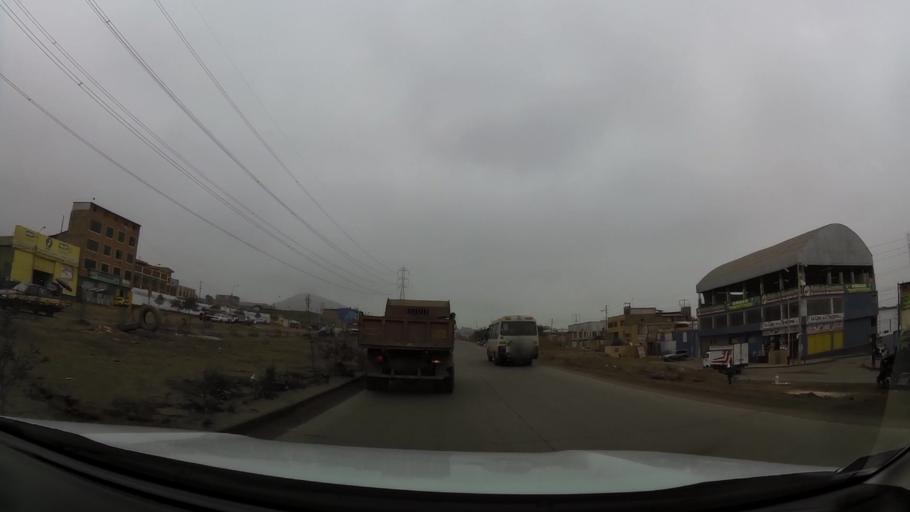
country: PE
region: Lima
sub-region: Lima
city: Surco
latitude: -12.1969
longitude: -76.9339
